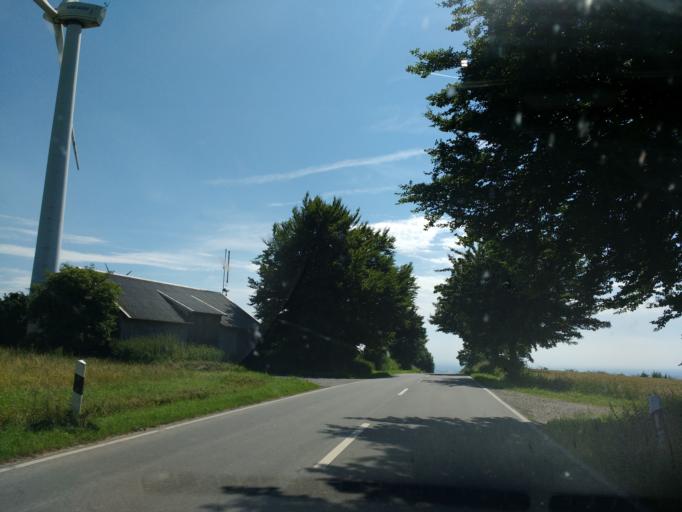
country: DE
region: North Rhine-Westphalia
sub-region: Regierungsbezirk Detmold
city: Horn
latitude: 51.8195
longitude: 8.9140
